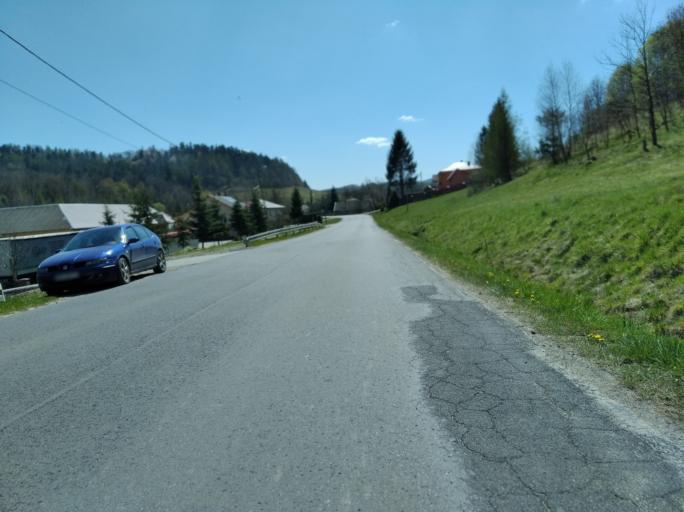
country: PL
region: Subcarpathian Voivodeship
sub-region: Powiat brzozowski
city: Dydnia
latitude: 49.6890
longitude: 22.1859
